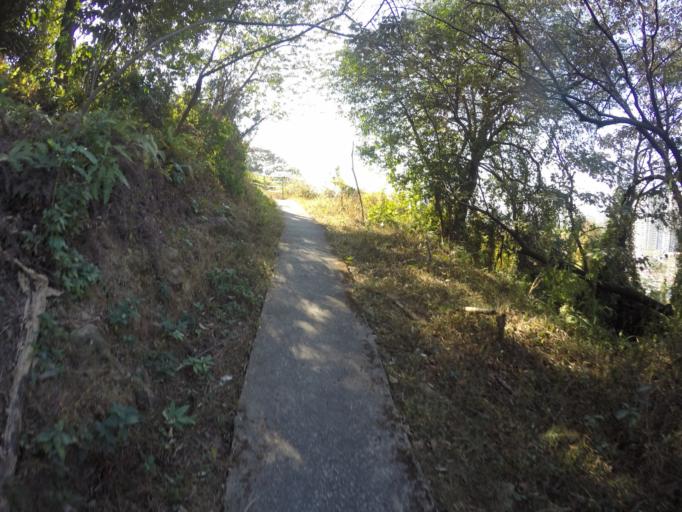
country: CN
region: Guangdong
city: Dongqu
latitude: 22.5335
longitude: 113.4031
